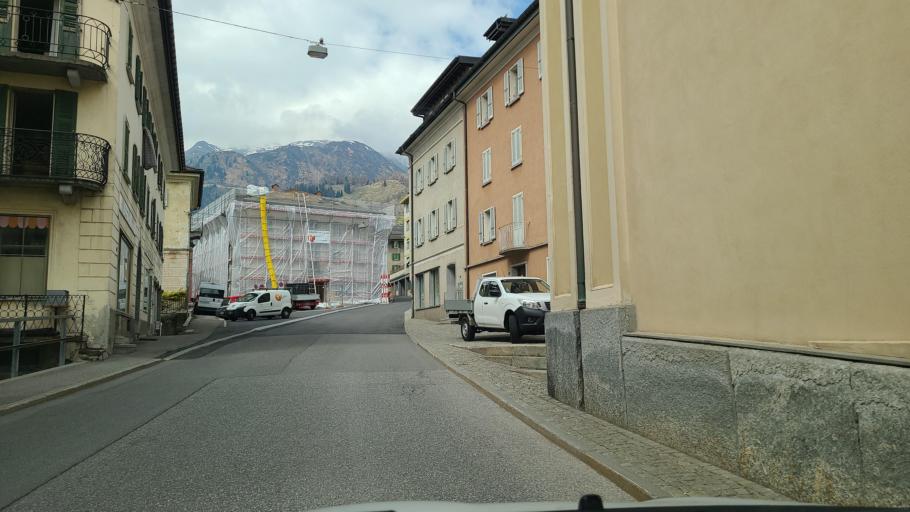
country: CH
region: Ticino
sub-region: Leventina District
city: Airolo
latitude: 46.5291
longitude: 8.6088
